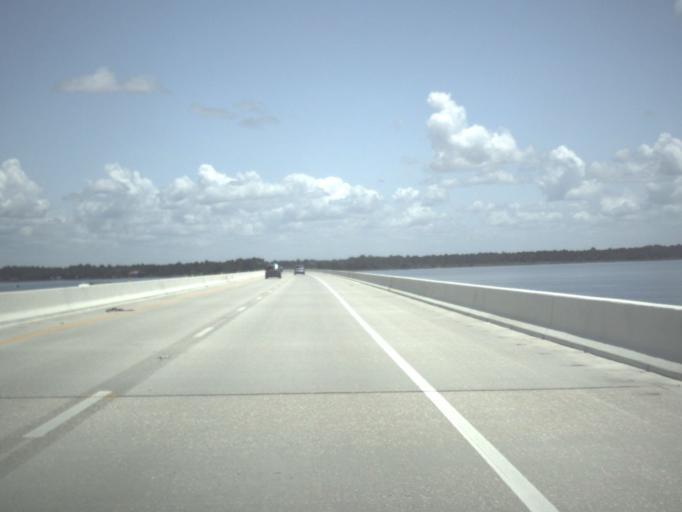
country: US
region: Florida
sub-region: Walton County
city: Freeport
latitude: 30.4201
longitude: -86.1588
